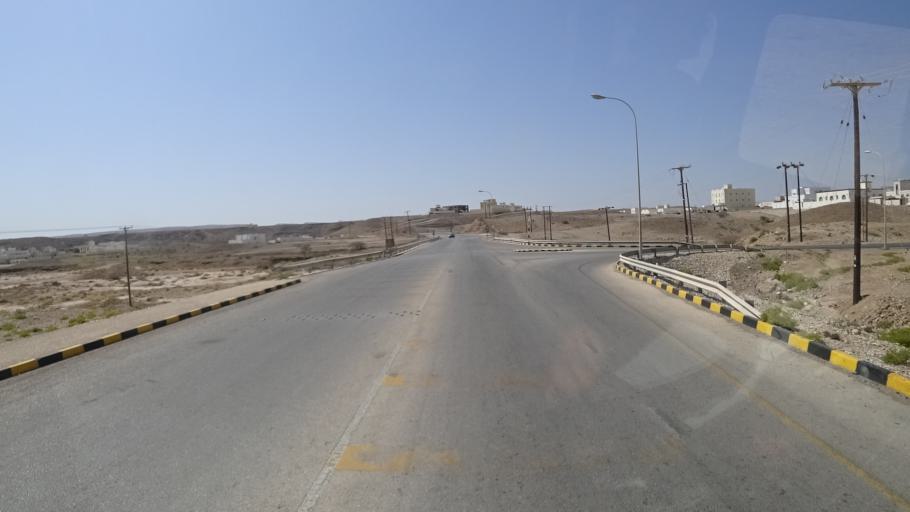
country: OM
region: Ash Sharqiyah
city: Sur
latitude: 22.5462
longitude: 59.5002
